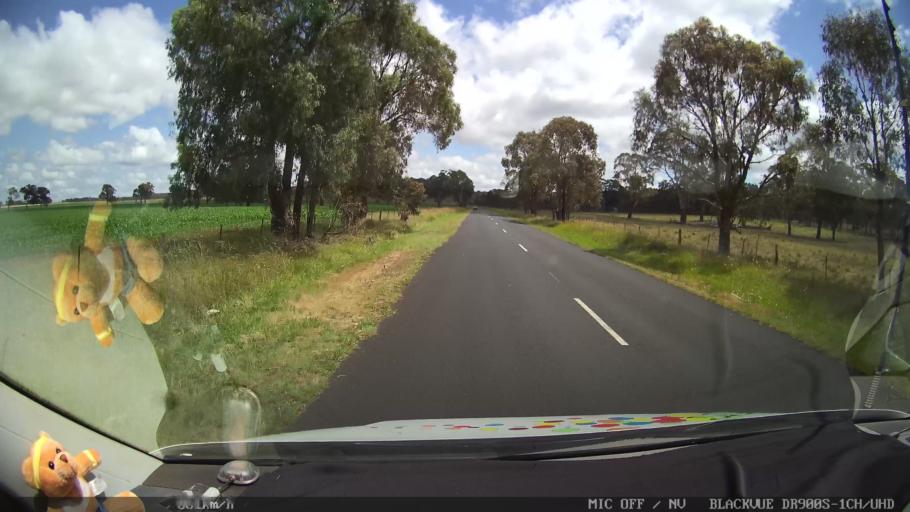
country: AU
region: New South Wales
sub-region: Glen Innes Severn
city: Glen Innes
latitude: -29.6022
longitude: 151.6666
